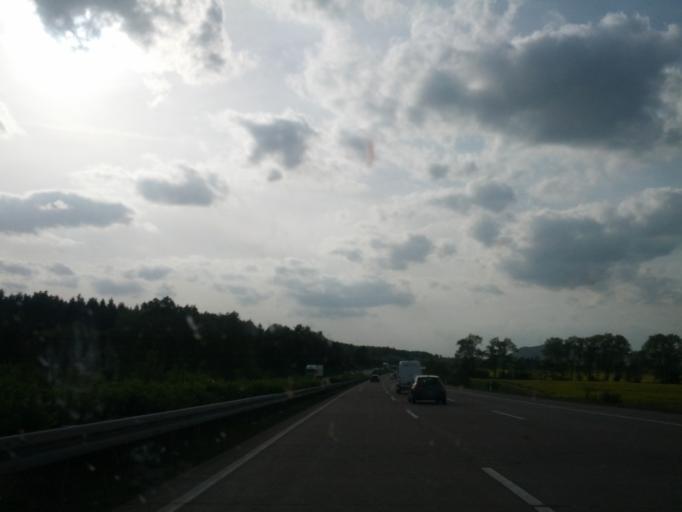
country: DE
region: Thuringia
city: Mechterstadt
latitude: 50.9228
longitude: 10.5232
